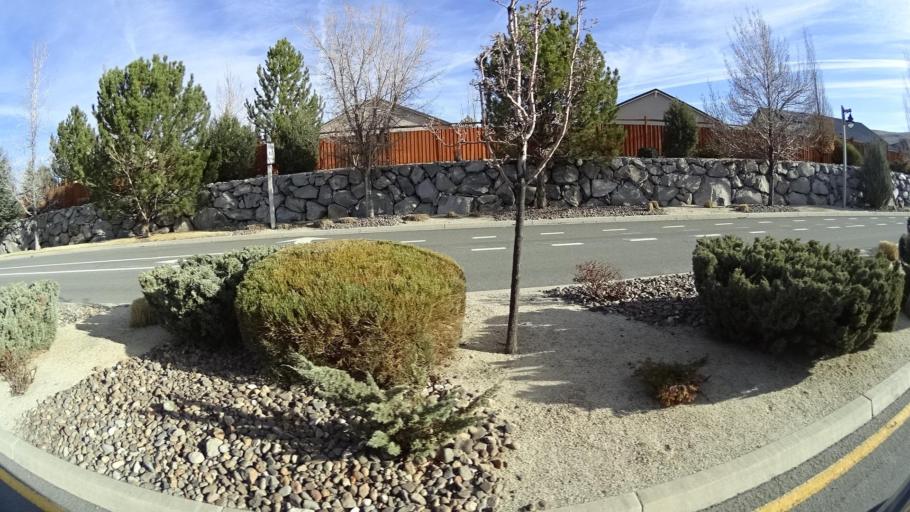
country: US
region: Nevada
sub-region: Washoe County
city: Spanish Springs
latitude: 39.6233
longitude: -119.6726
